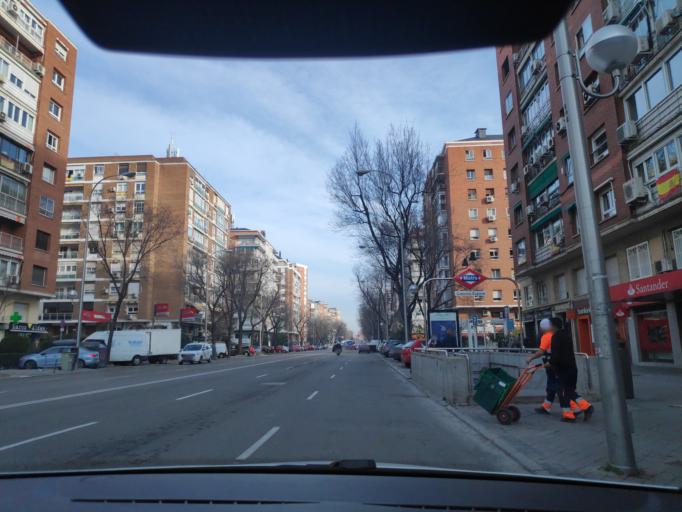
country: ES
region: Madrid
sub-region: Provincia de Madrid
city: Chamartin
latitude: 40.4496
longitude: -3.6777
